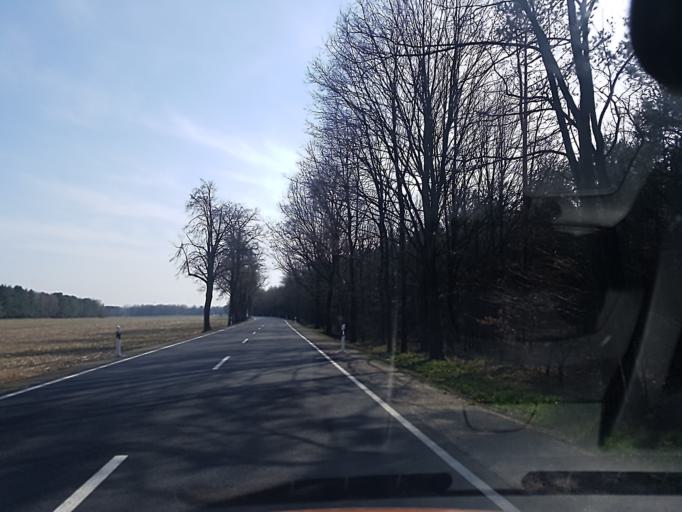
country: DE
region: Brandenburg
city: Bronkow
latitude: 51.6842
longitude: 13.9155
